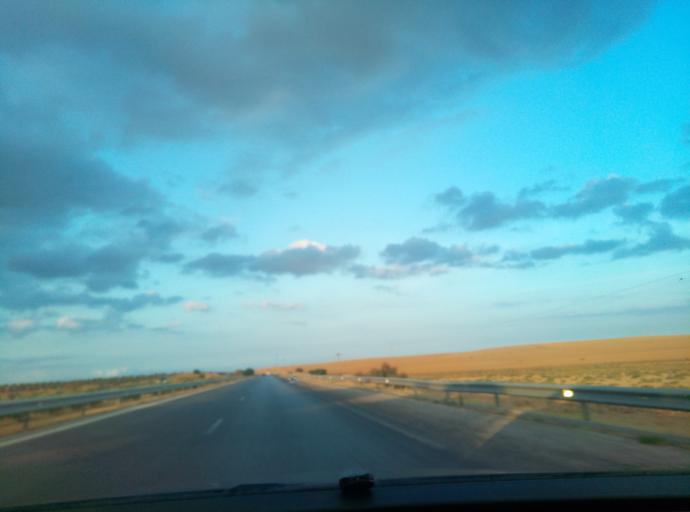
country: TN
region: Manouba
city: El Battan
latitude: 36.7052
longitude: 9.9598
